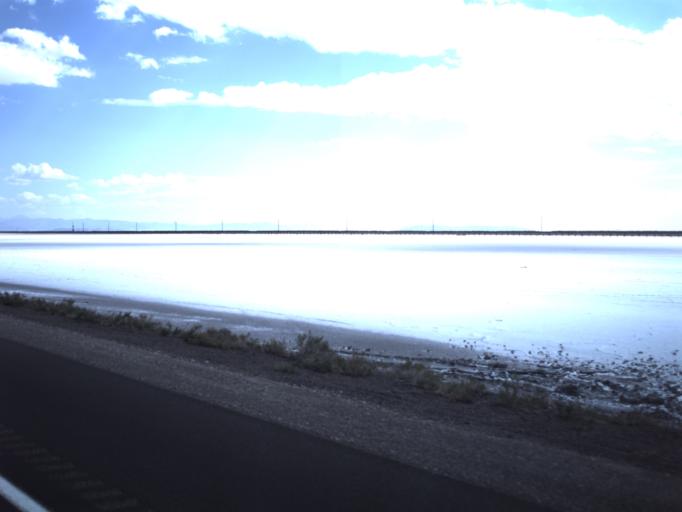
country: US
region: Utah
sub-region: Tooele County
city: Wendover
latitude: 40.7339
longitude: -113.6345
